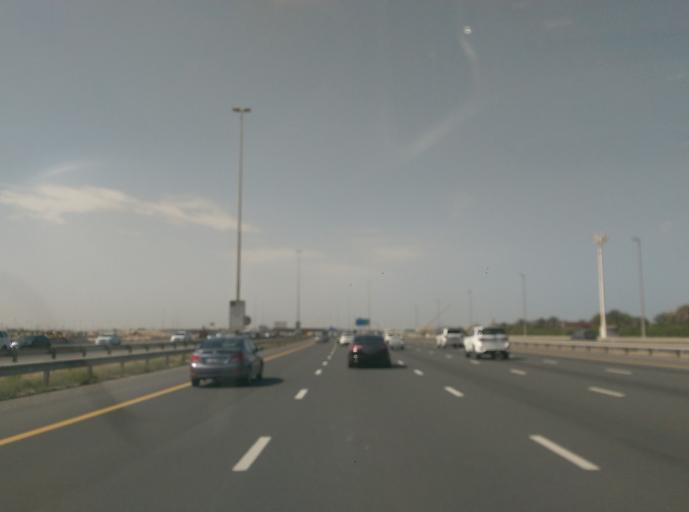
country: AE
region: Dubai
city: Dubai
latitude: 25.1743
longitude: 55.2728
